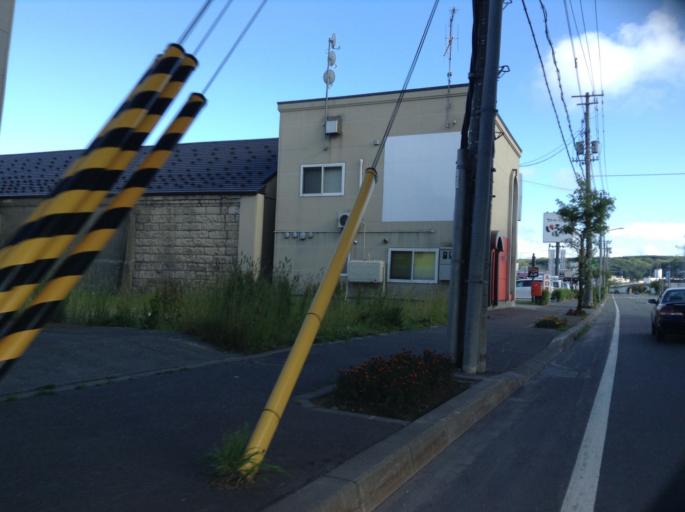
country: JP
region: Hokkaido
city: Wakkanai
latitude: 45.4095
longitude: 141.6758
